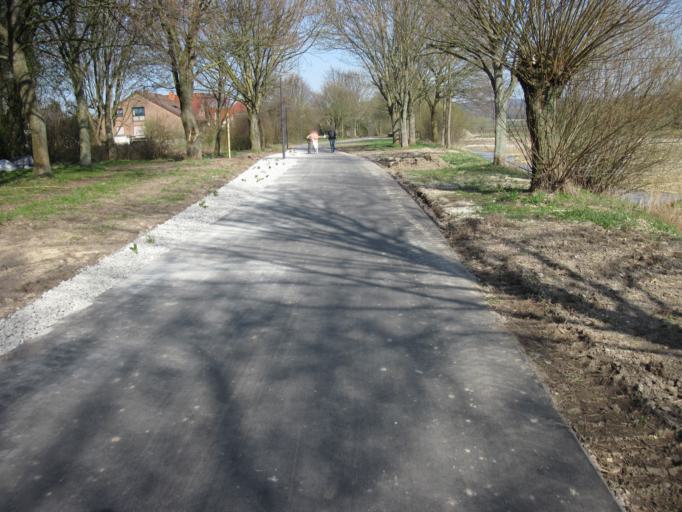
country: DE
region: North Rhine-Westphalia
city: Bad Lippspringe
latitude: 51.7895
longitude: 8.8306
